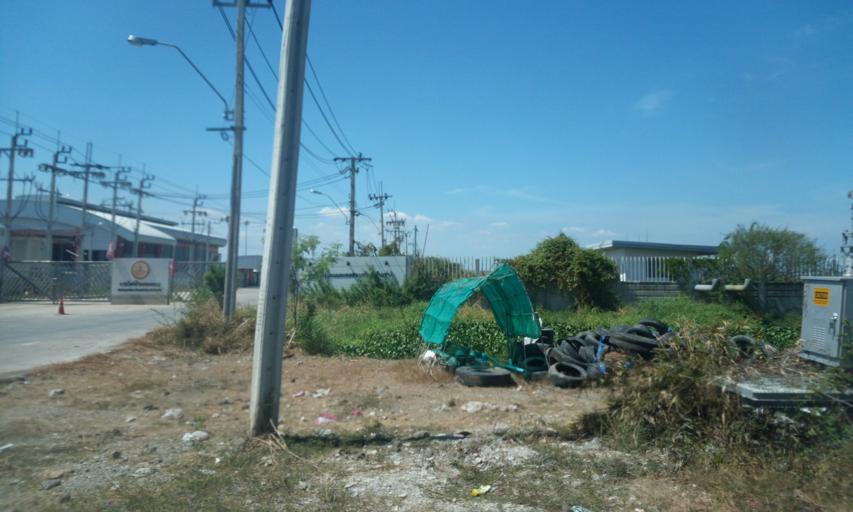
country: TH
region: Samut Prakan
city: Bang Bo District
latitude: 13.5561
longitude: 100.7708
